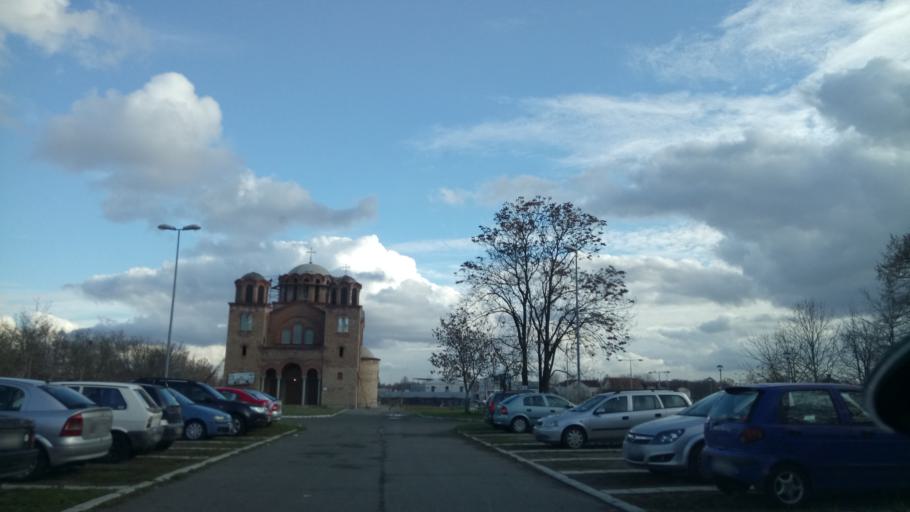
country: RS
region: Central Serbia
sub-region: Belgrade
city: Zemun
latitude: 44.8608
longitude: 20.3729
